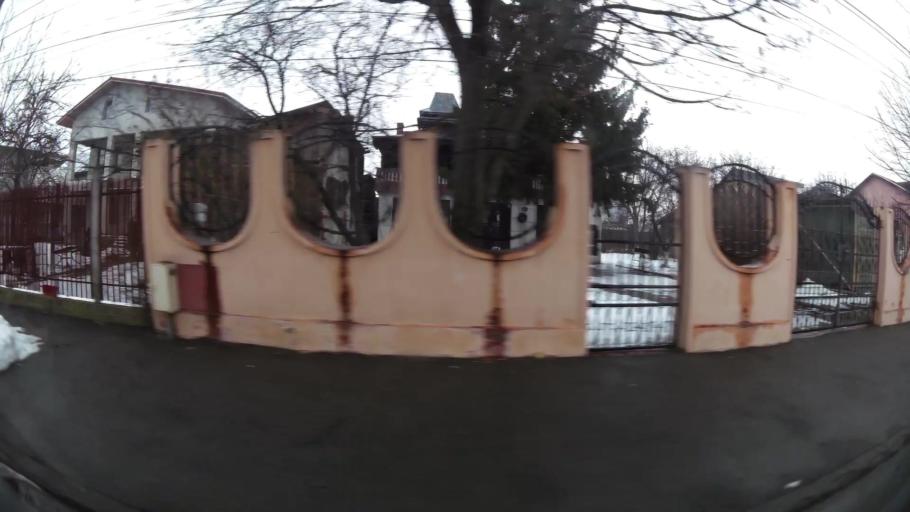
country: RO
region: Ilfov
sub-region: Comuna Mogosoaia
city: Mogosoaia
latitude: 44.5134
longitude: 26.0202
